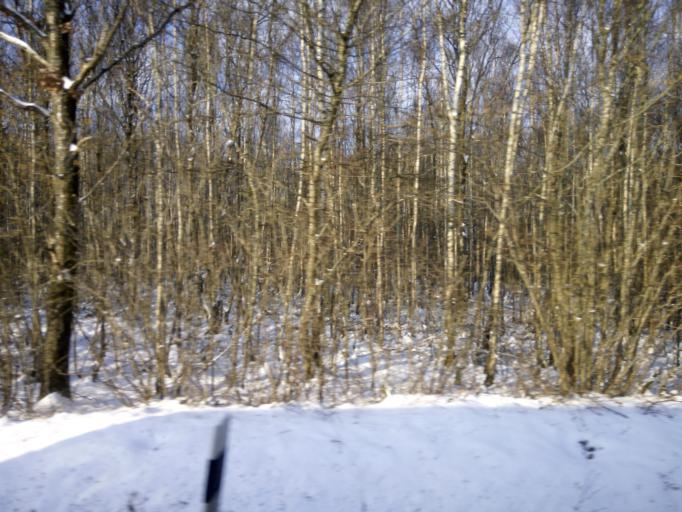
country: LU
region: Grevenmacher
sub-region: Canton d'Echternach
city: Consdorf
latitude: 49.7917
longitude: 6.3455
